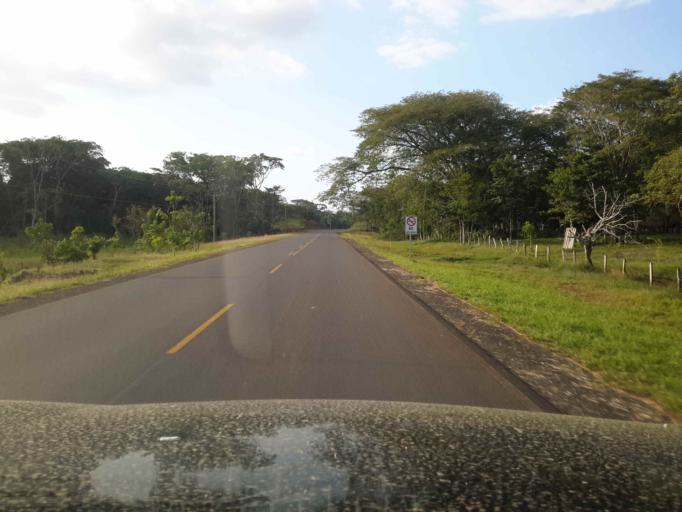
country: NI
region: Rio San Juan
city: San Carlos
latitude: 11.1706
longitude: -84.6725
